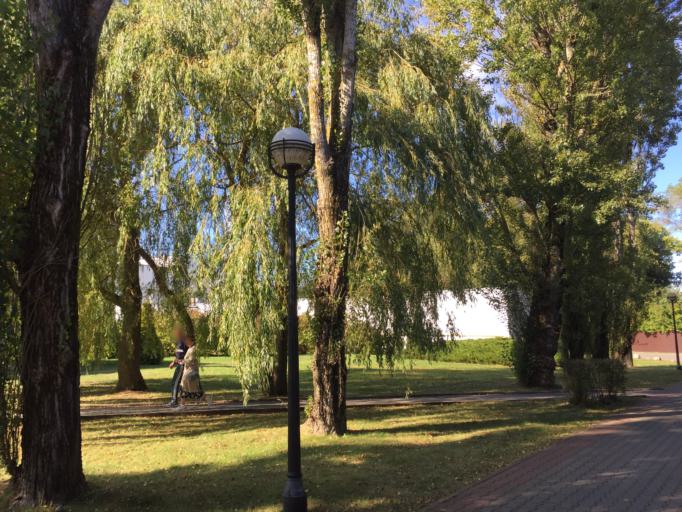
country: RU
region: Kaliningrad
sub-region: Gorod Svetlogorsk
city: Svetlogorsk
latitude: 54.9434
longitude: 20.1373
